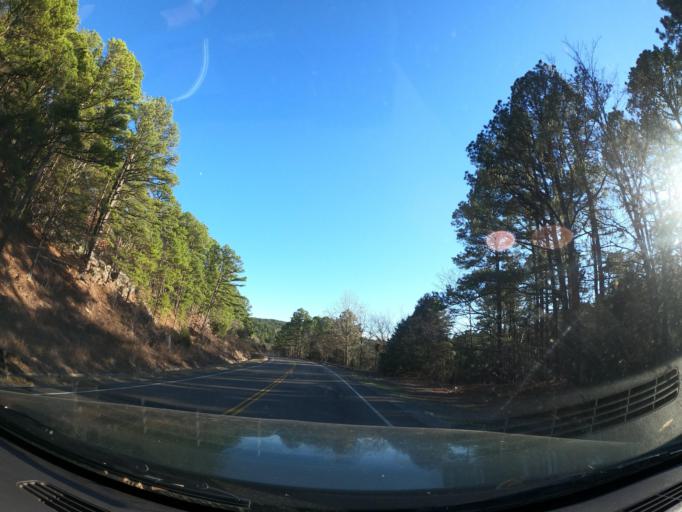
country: US
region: Oklahoma
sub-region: Latimer County
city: Wilburton
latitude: 34.9757
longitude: -95.3587
